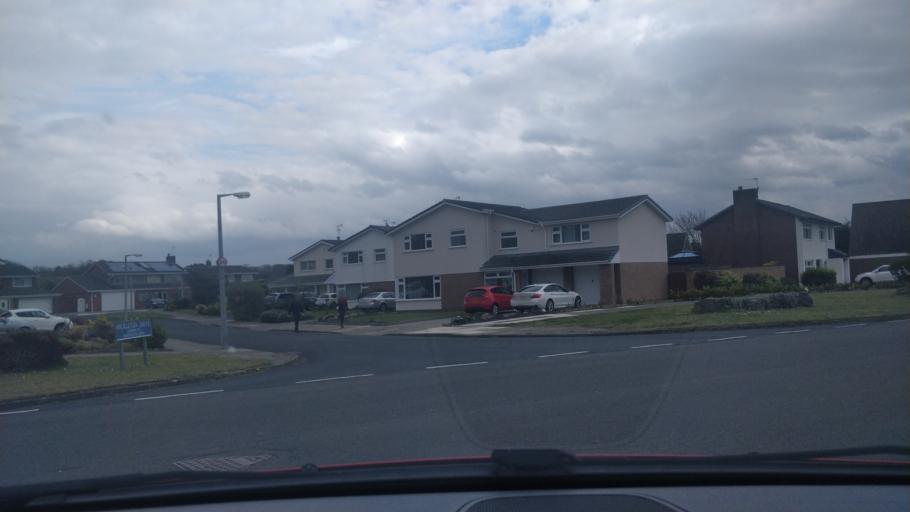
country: GB
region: England
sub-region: Sefton
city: Formby
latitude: 53.6043
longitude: -3.0525
